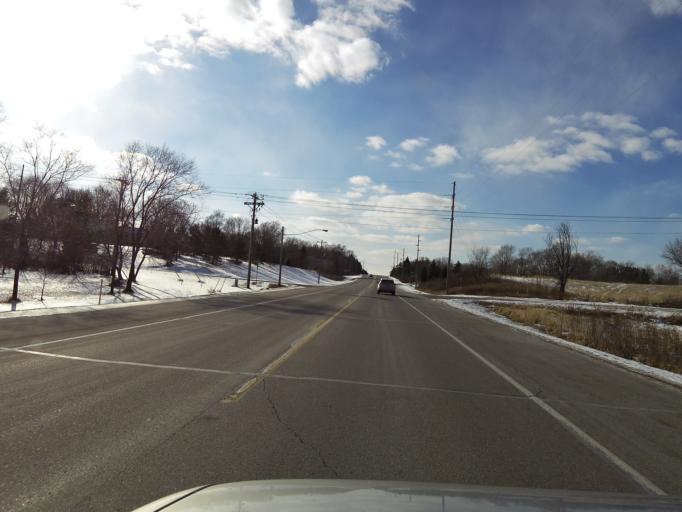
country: US
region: Minnesota
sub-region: Dakota County
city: Rosemount
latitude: 44.7682
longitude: -93.1281
